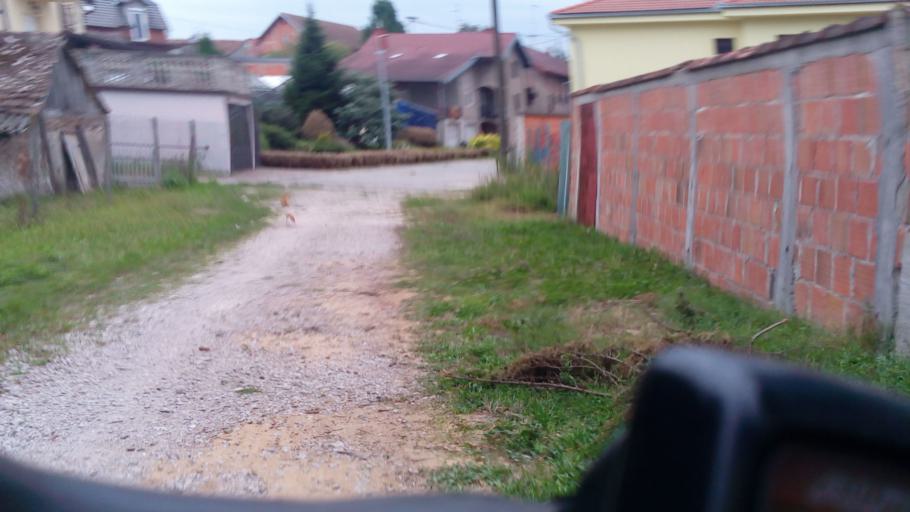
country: HR
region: Vukovarsko-Srijemska
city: Vinkovci
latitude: 45.2877
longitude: 18.8093
